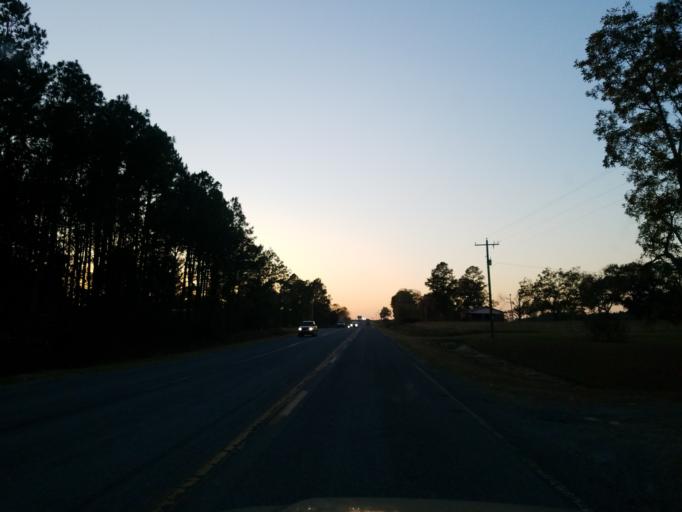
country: US
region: Georgia
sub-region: Ben Hill County
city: Fitzgerald
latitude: 31.7201
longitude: -83.4029
